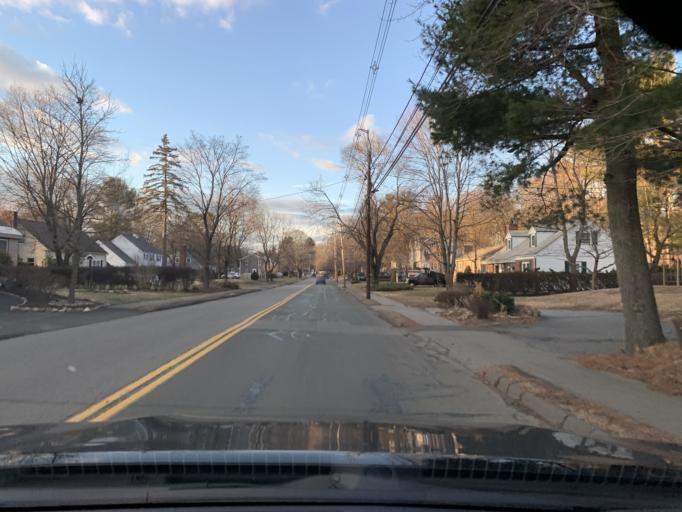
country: US
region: Massachusetts
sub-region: Essex County
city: Lynnfield
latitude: 42.5182
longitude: -71.0150
